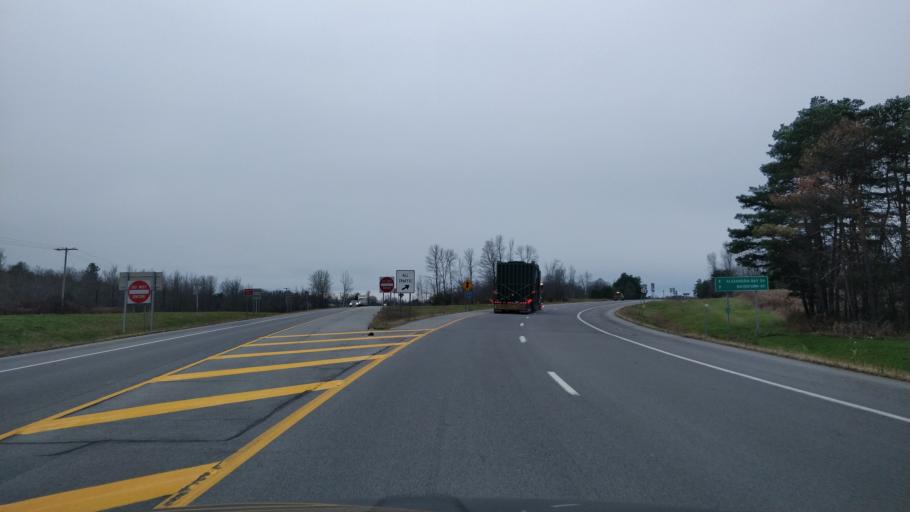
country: CA
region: Ontario
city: Brockville
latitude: 44.5782
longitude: -75.6414
